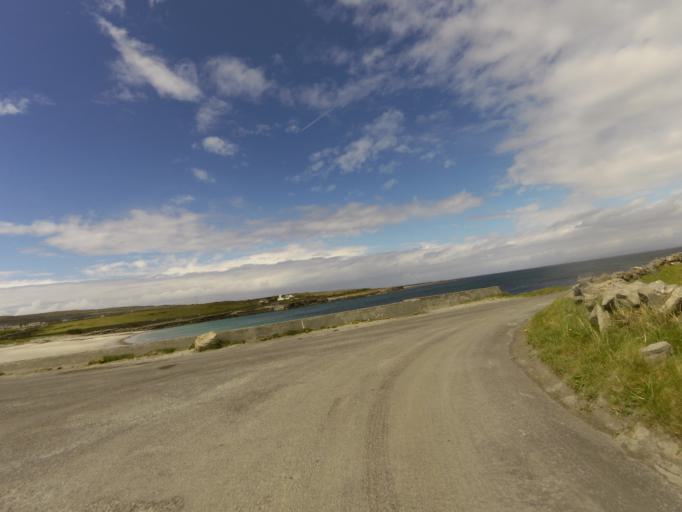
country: IE
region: Connaught
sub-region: County Galway
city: Clifden
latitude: 53.1309
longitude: -9.7468
